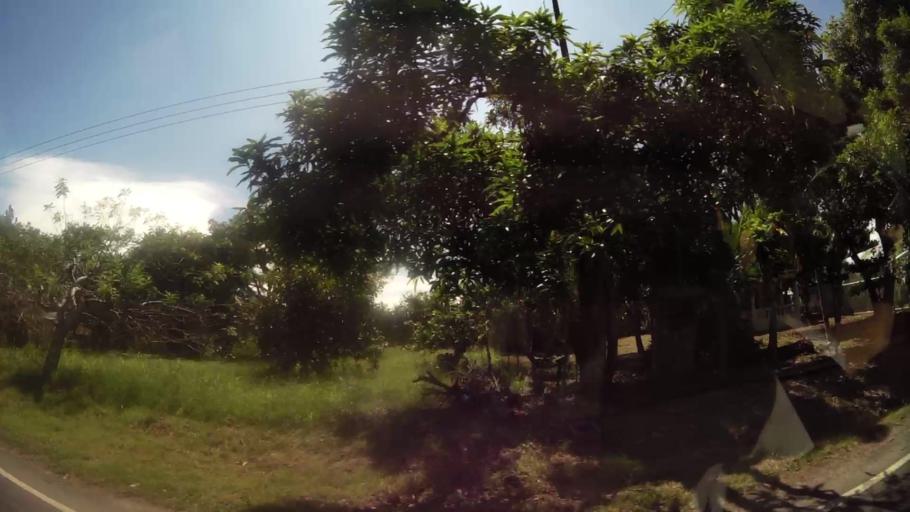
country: PA
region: Panama
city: Nueva Gorgona
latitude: 8.5591
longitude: -79.8873
